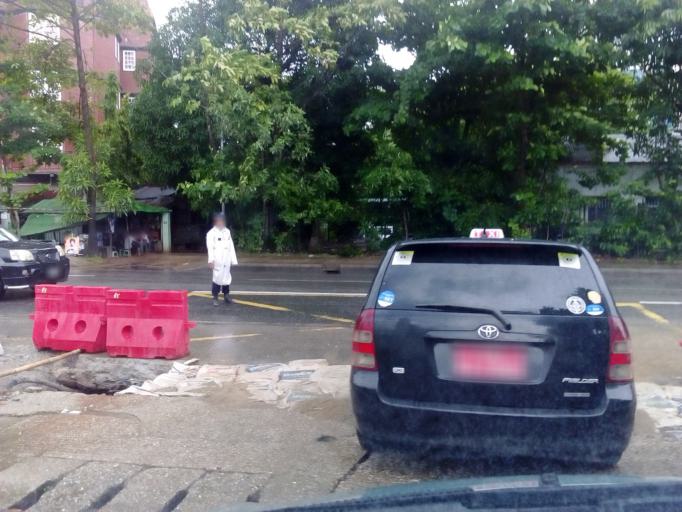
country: MM
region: Yangon
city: Yangon
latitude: 16.8238
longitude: 96.1521
